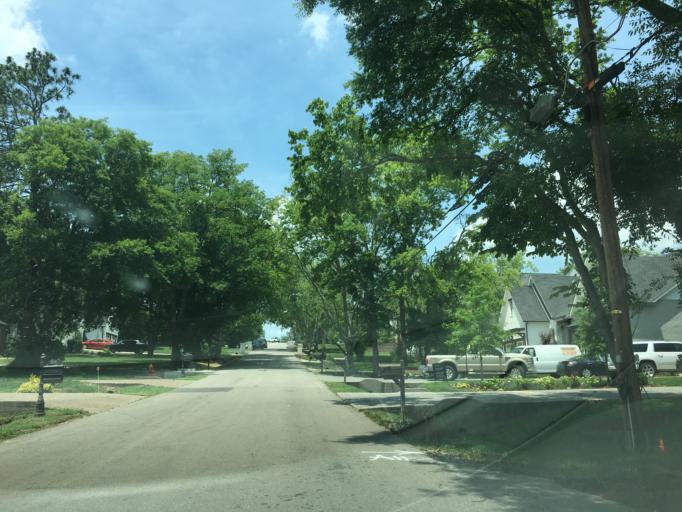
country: US
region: Tennessee
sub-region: Davidson County
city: Belle Meade
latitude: 36.1002
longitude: -86.8261
